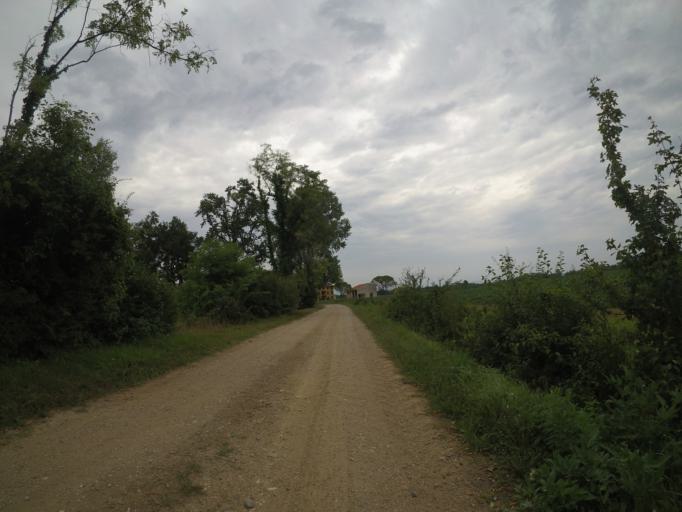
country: IT
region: Friuli Venezia Giulia
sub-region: Provincia di Udine
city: Rivignano
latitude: 45.8991
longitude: 13.0622
